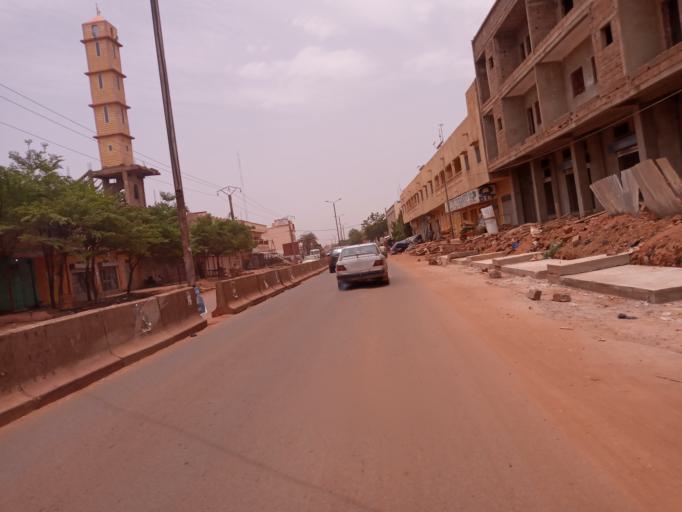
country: ML
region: Bamako
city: Bamako
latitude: 12.5889
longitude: -8.0214
